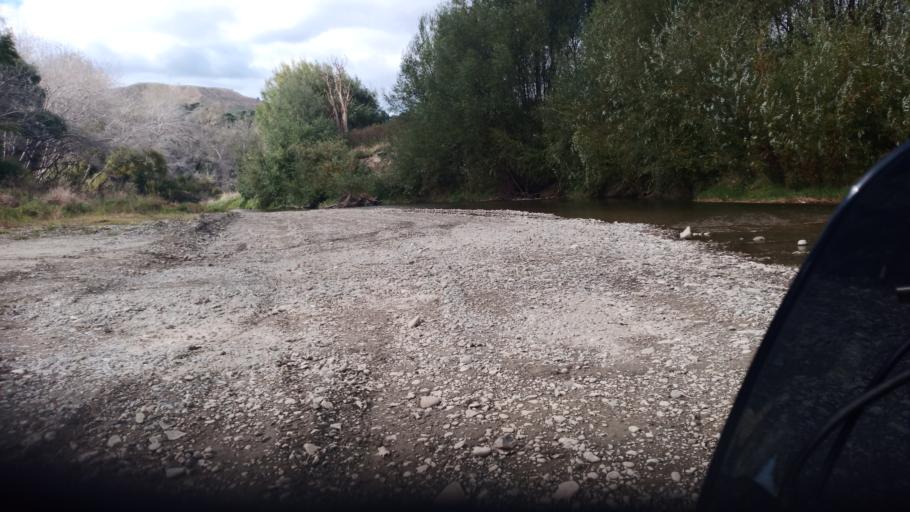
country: NZ
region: Gisborne
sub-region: Gisborne District
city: Gisborne
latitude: -38.4383
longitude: 177.7467
